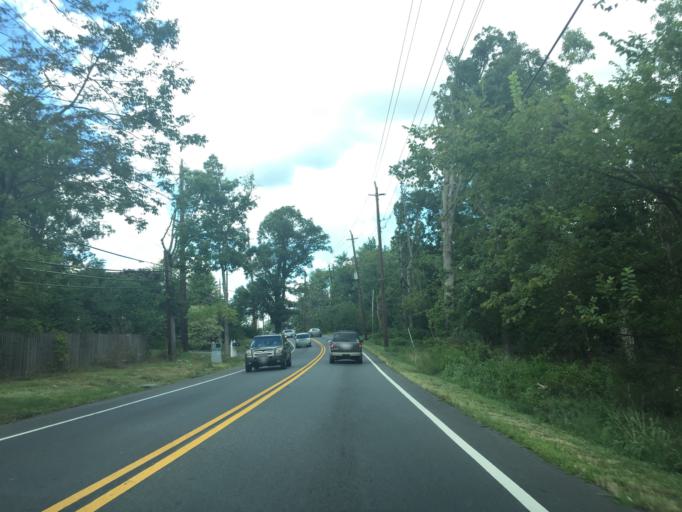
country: US
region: Maryland
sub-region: Montgomery County
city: Redland
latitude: 39.1562
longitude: -77.1564
